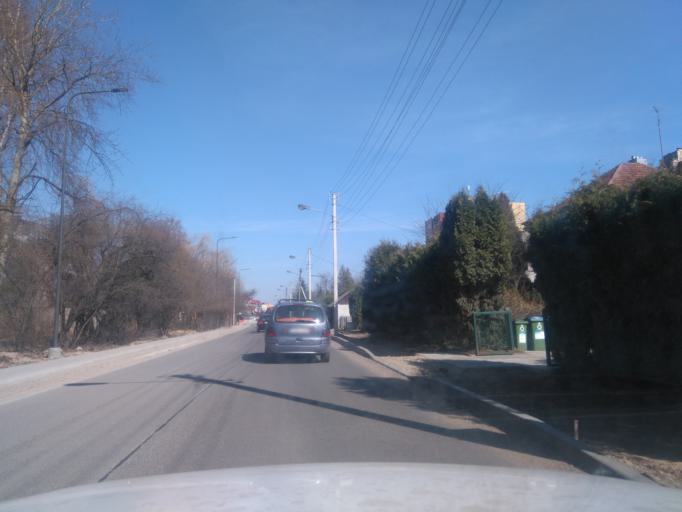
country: LT
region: Kauno apskritis
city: Dainava (Kaunas)
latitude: 54.8911
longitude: 23.9545
